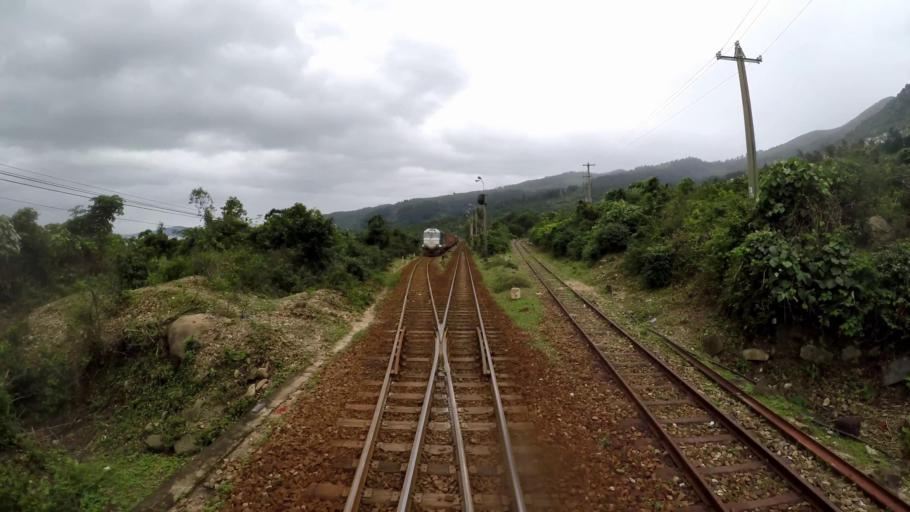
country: VN
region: Da Nang
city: Lien Chieu
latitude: 16.1682
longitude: 108.1361
